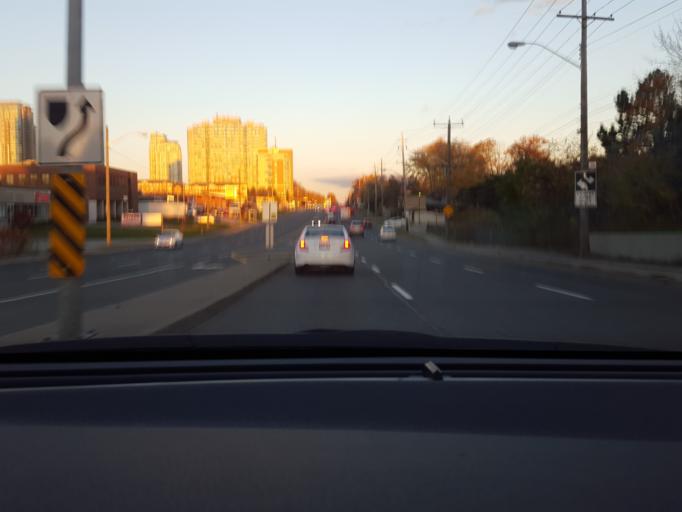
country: CA
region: Ontario
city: Scarborough
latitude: 43.7690
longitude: -79.2664
